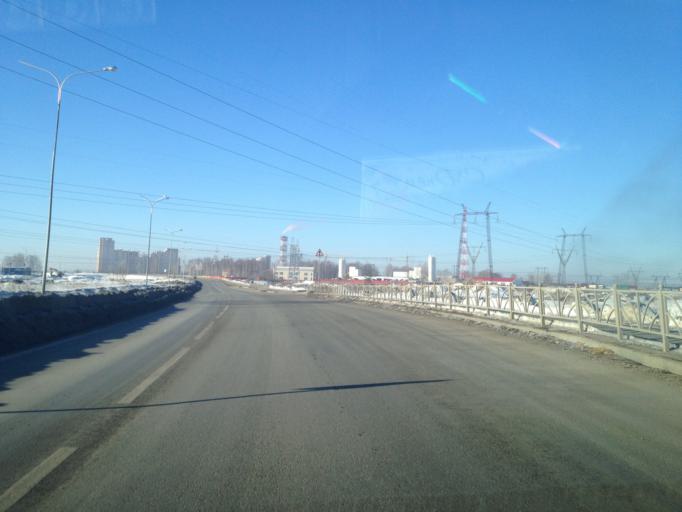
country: RU
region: Sverdlovsk
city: Sovkhoznyy
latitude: 56.7530
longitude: 60.5827
